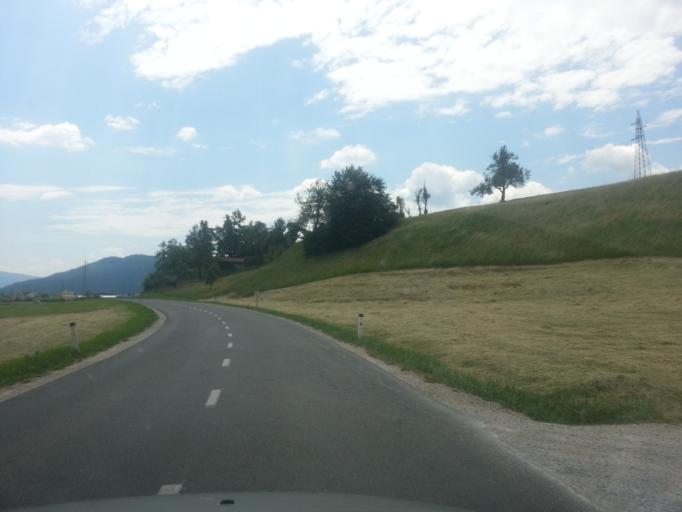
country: SI
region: Vrhnika
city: Vrhnika
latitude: 45.9812
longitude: 14.2878
